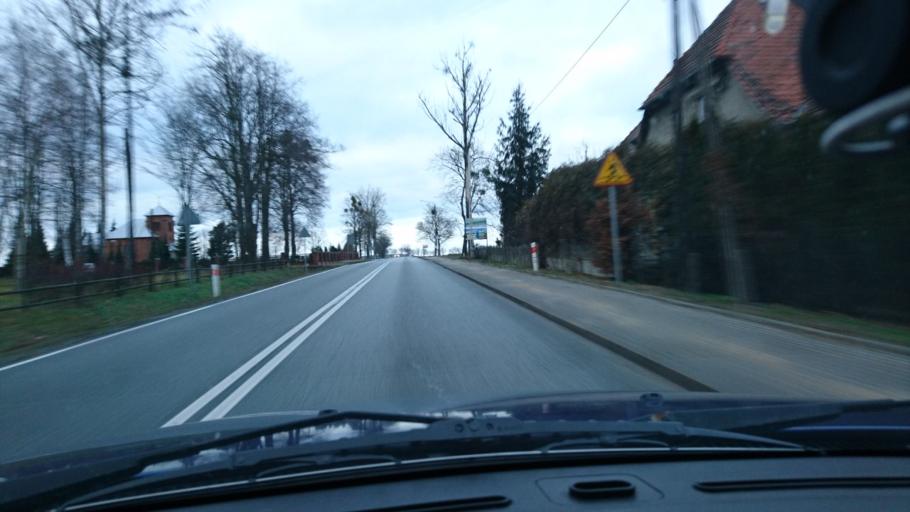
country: PL
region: Opole Voivodeship
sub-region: Powiat kluczborski
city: Byczyna
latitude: 51.0645
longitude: 18.2013
